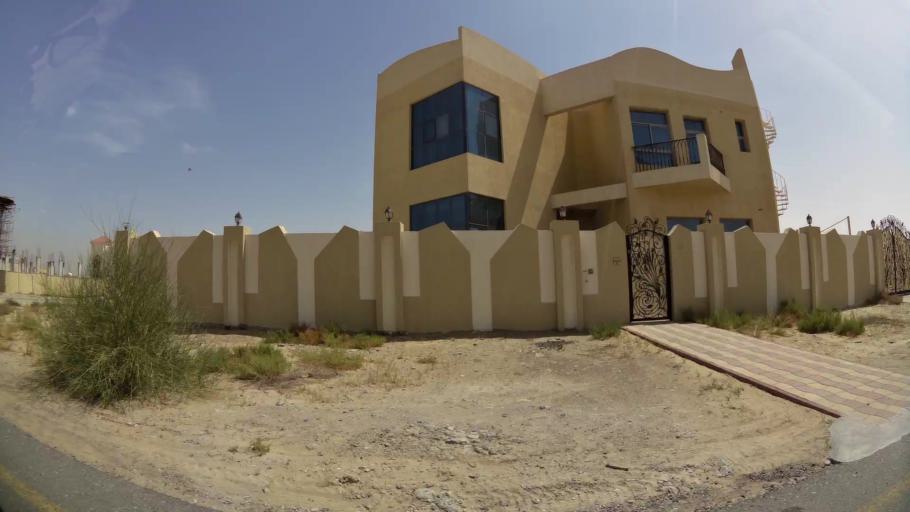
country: AE
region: Ash Shariqah
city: Sharjah
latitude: 25.1831
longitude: 55.4321
